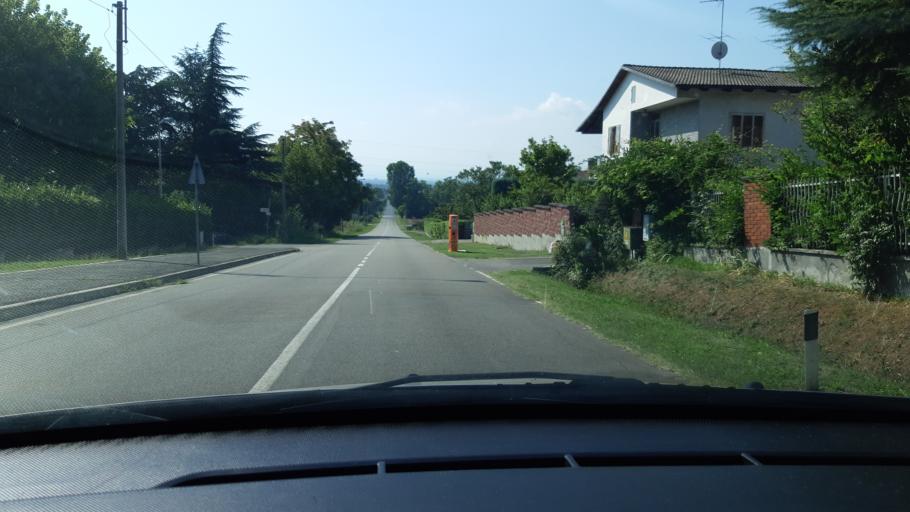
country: IT
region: Piedmont
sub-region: Provincia di Alessandria
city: Castelletto Monferrato
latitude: 44.9752
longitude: 8.5721
